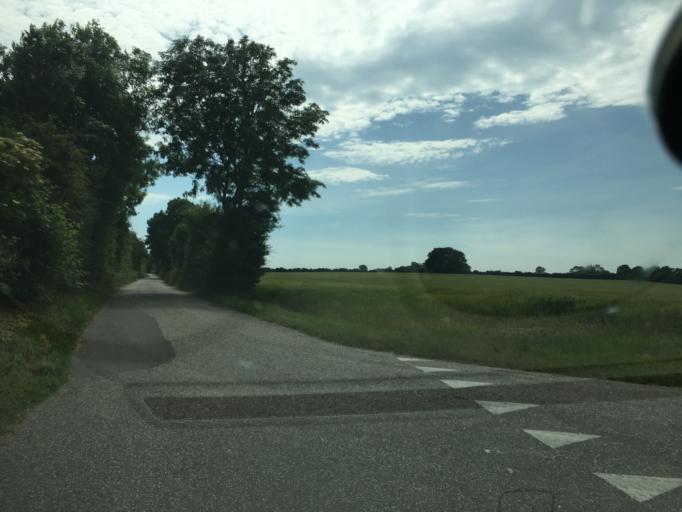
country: DK
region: South Denmark
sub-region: Sonderborg Kommune
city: Dybbol
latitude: 54.9460
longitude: 9.7451
